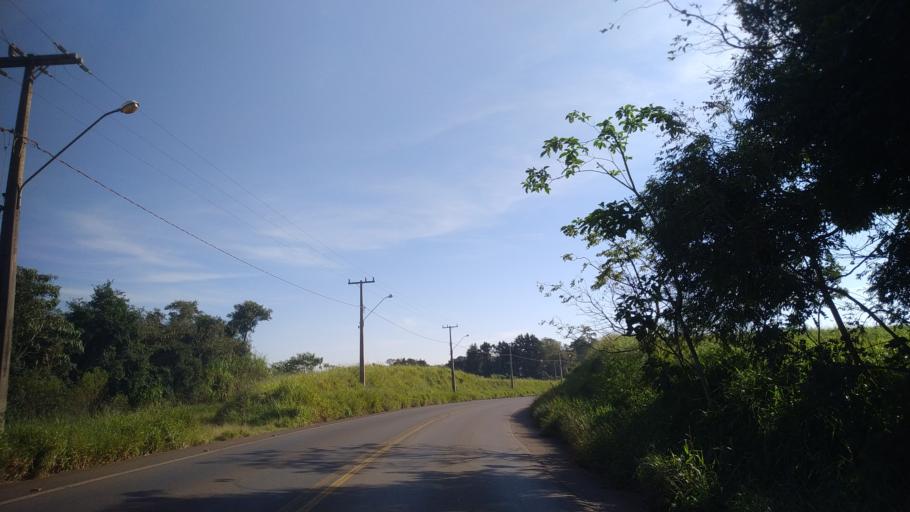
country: BR
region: Santa Catarina
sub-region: Chapeco
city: Chapeco
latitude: -27.1237
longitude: -52.6337
